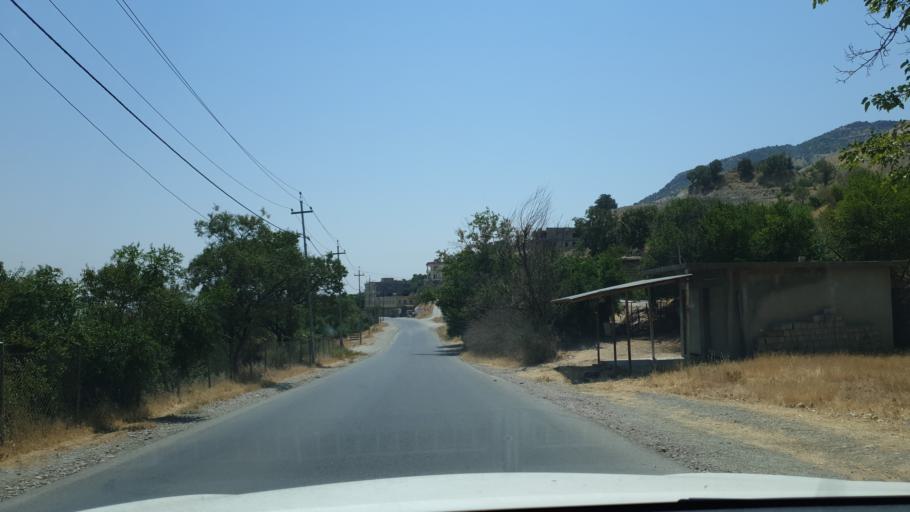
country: IQ
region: Arbil
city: Nahiyat Hiran
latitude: 36.2851
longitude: 44.4883
